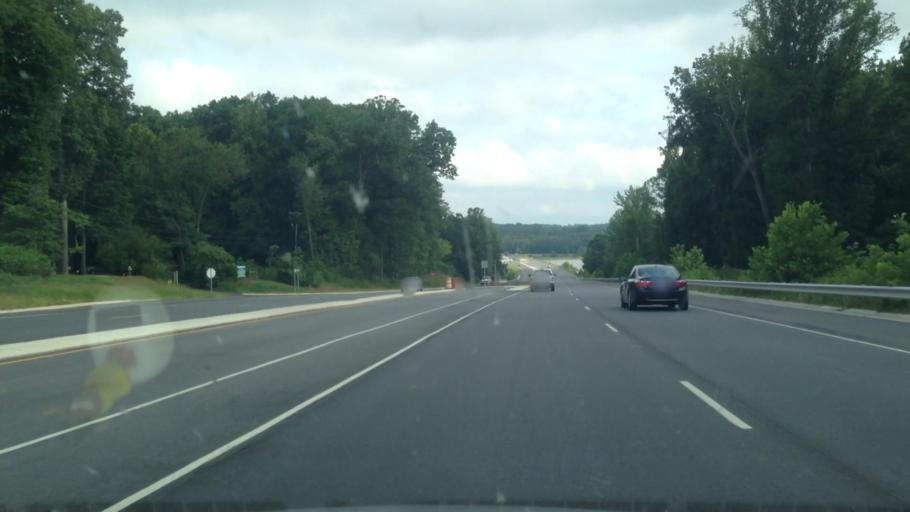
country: US
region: North Carolina
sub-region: Guilford County
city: Summerfield
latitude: 36.1656
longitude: -79.8783
